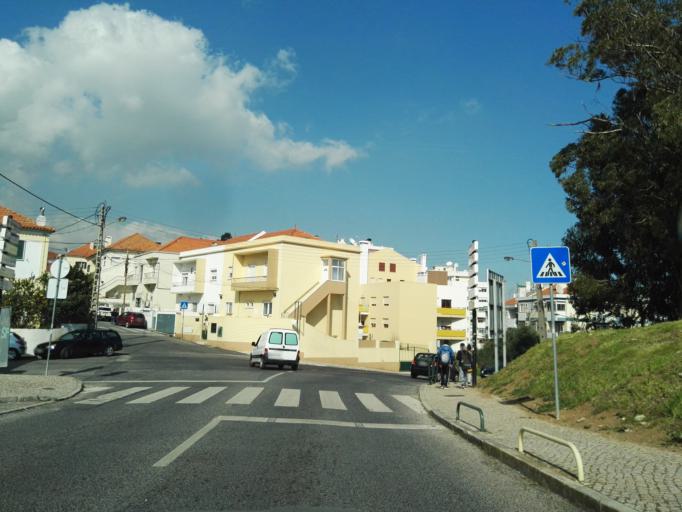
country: PT
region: Lisbon
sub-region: Odivelas
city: Povoa de Santo Adriao
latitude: 38.8019
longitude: -9.1650
